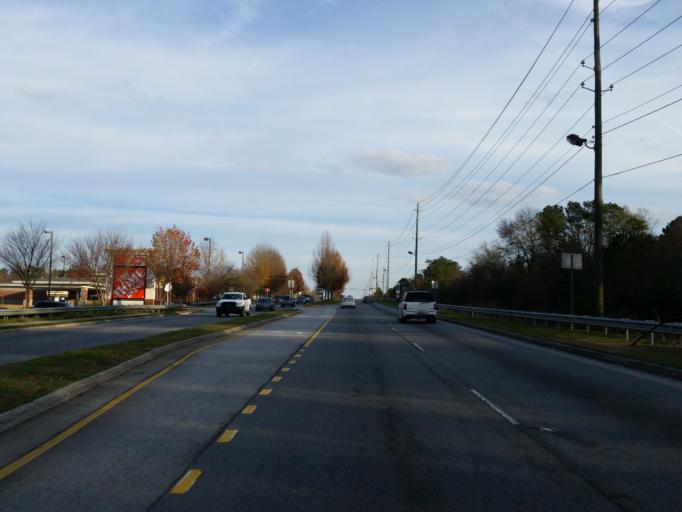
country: US
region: Georgia
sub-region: Cobb County
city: Powder Springs
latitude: 33.8642
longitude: -84.6799
